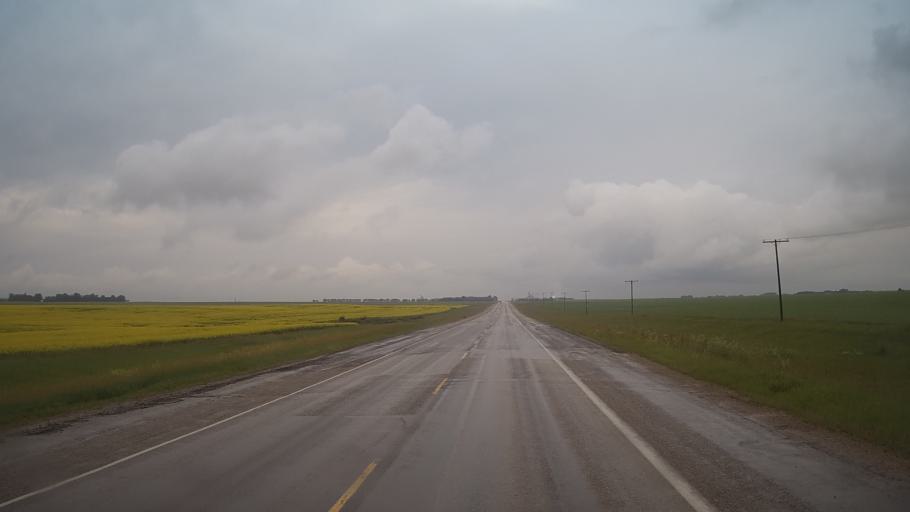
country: CA
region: Saskatchewan
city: Unity
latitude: 52.4350
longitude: -109.0530
